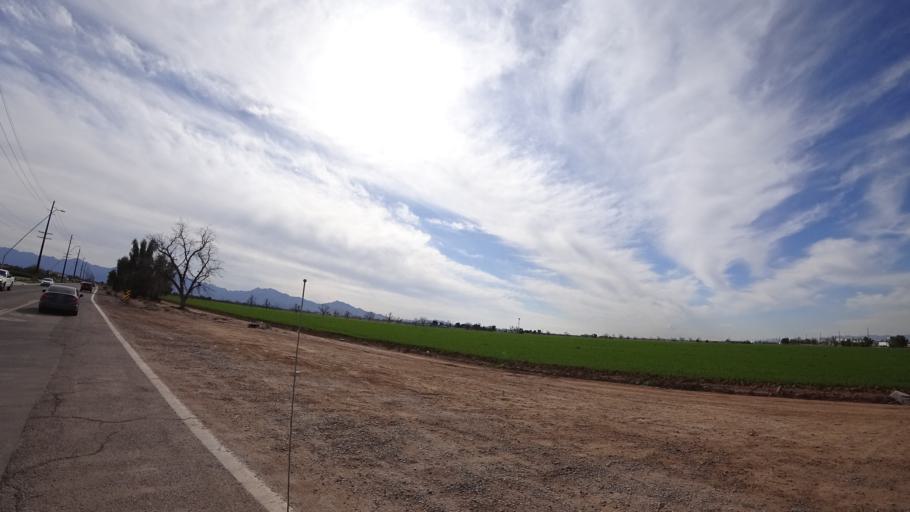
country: US
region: Arizona
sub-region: Maricopa County
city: Tolleson
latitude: 33.4344
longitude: -112.2552
